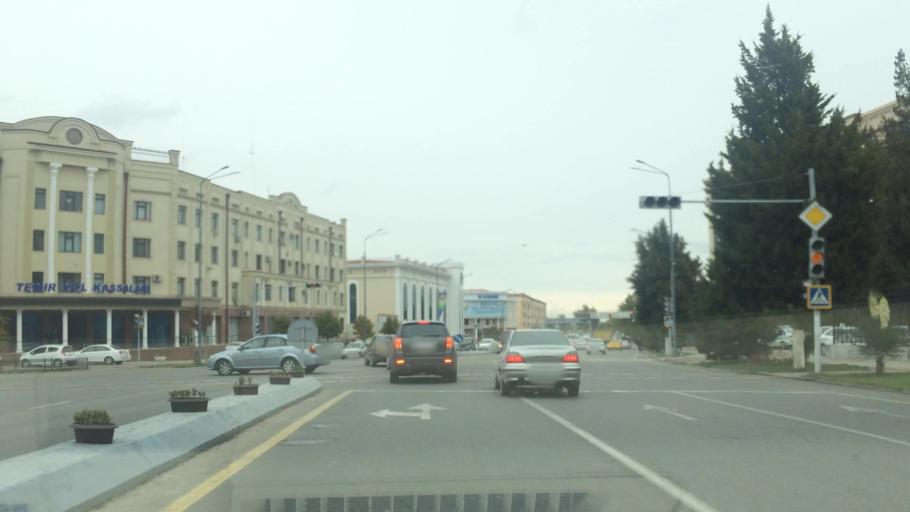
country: UZ
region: Samarqand
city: Samarqand
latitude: 39.6537
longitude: 66.9618
